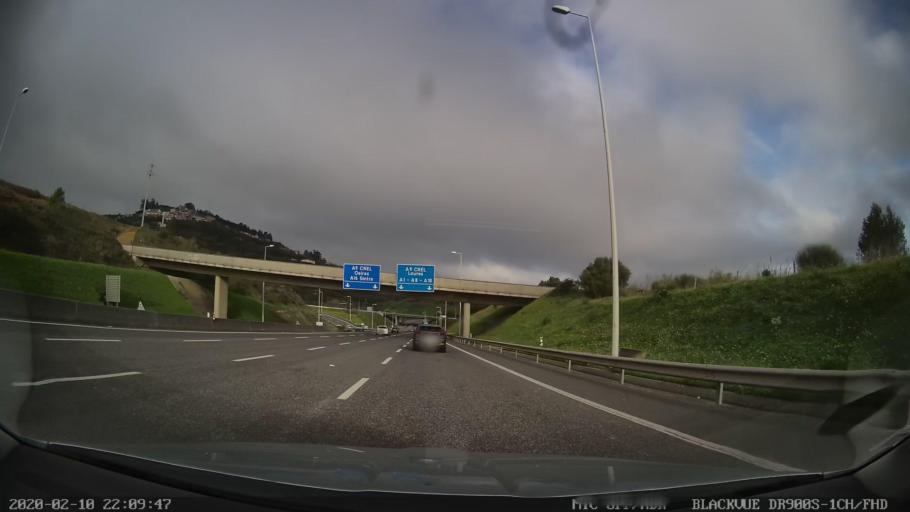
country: PT
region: Lisbon
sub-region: Odivelas
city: Ramada
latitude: 38.8226
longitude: -9.1896
